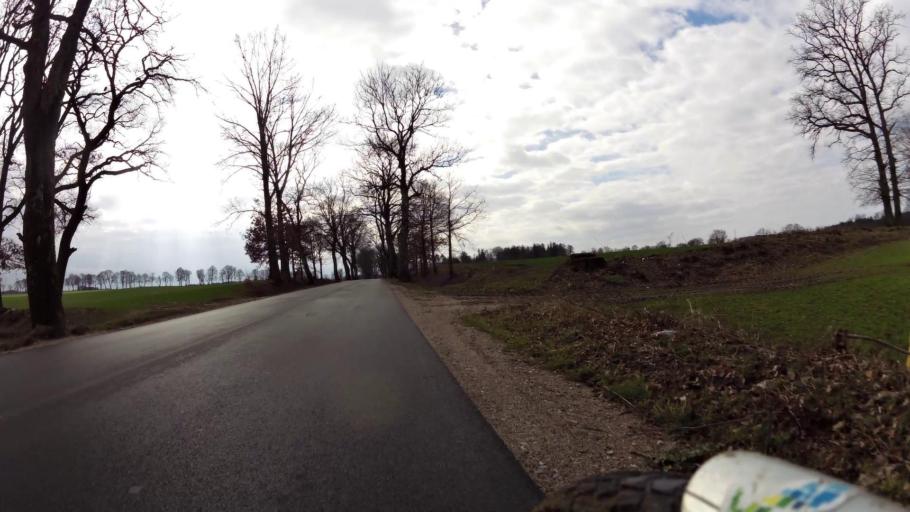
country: PL
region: Pomeranian Voivodeship
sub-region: Powiat bytowski
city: Kolczyglowy
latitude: 54.2240
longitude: 17.2407
